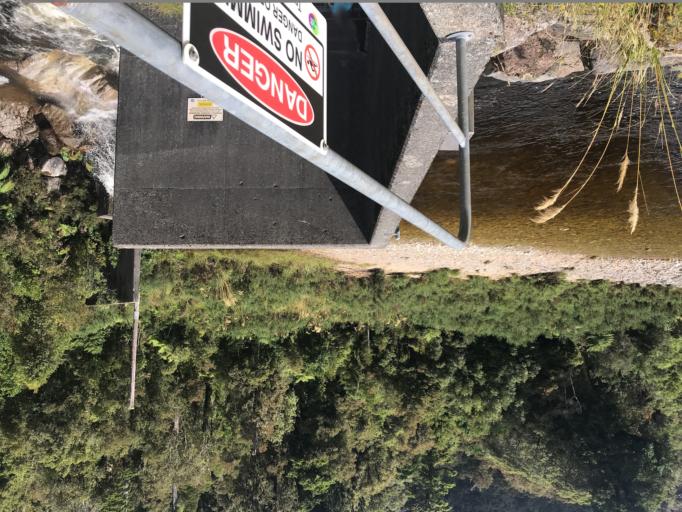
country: NZ
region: West Coast
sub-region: Westland District
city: Hokitika
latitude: -42.7559
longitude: 171.2252
